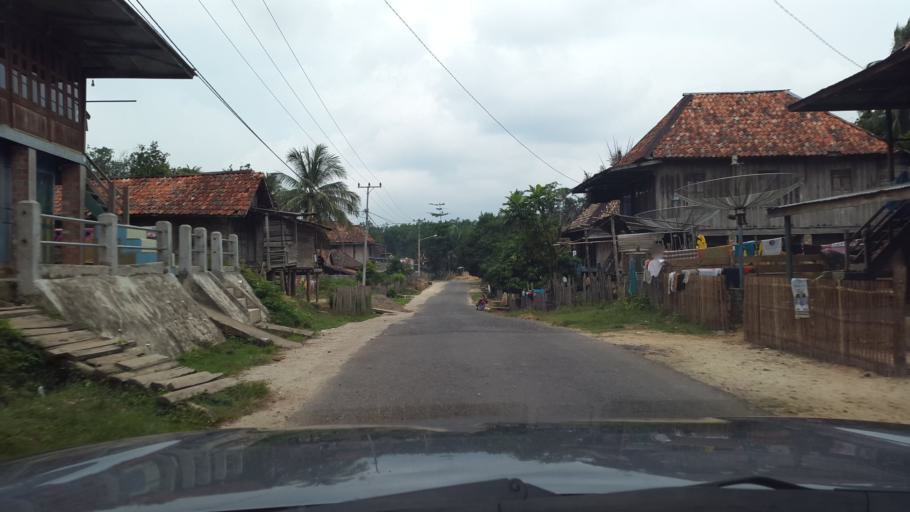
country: ID
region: South Sumatra
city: Gunungmenang
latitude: -3.1178
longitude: 103.8621
